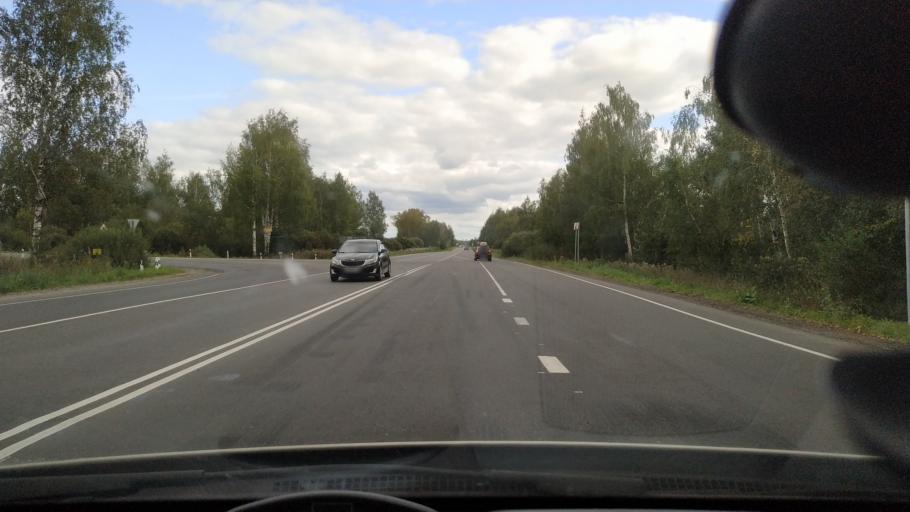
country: RU
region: Moskovskaya
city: Drezna
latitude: 55.7234
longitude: 38.8438
